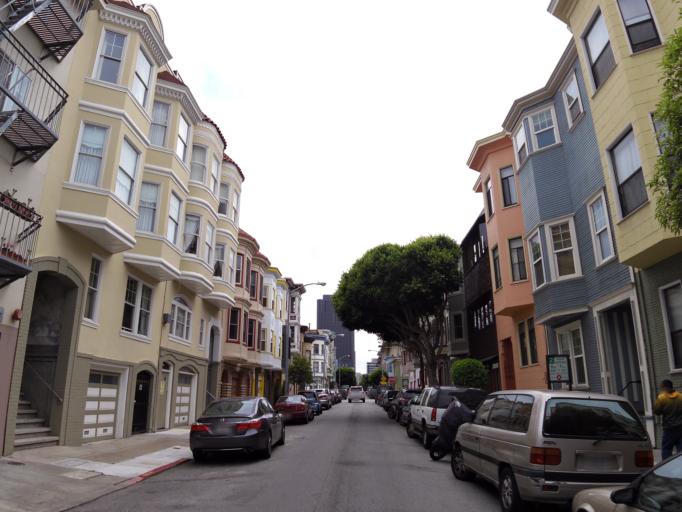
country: US
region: California
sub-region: San Francisco County
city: San Francisco
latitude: 37.8006
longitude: -122.4060
